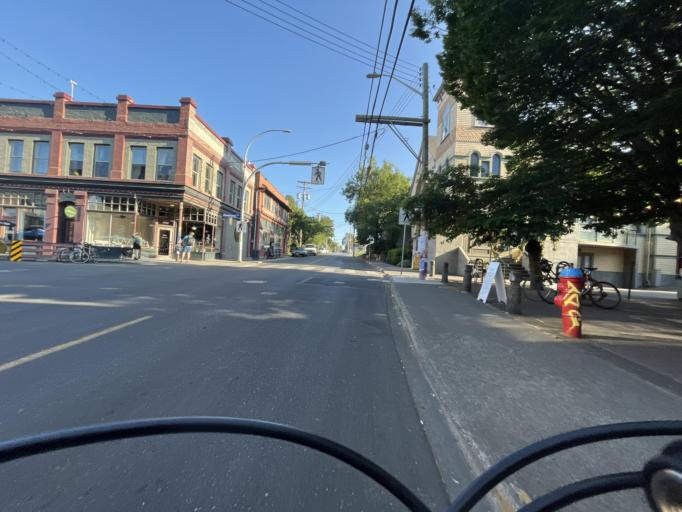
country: CA
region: British Columbia
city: Victoria
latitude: 48.4305
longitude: -123.3452
